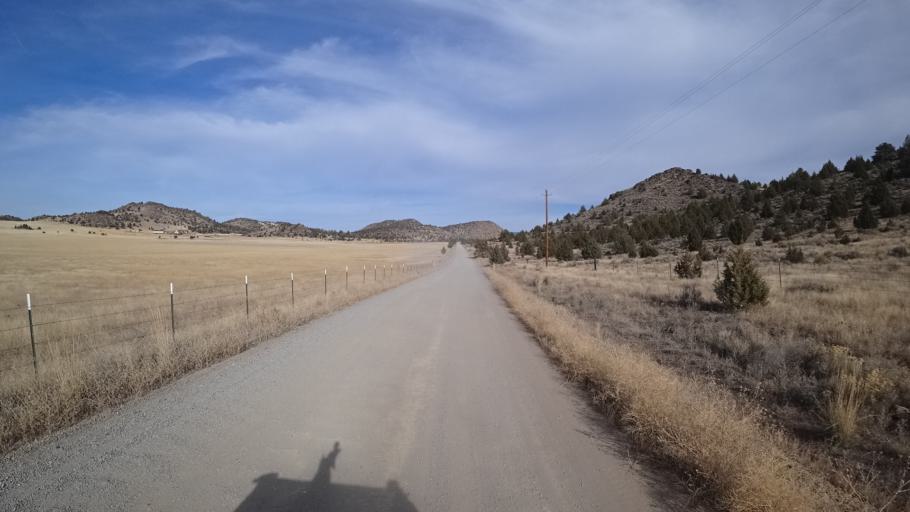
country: US
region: California
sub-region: Siskiyou County
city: Weed
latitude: 41.5693
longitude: -122.4681
